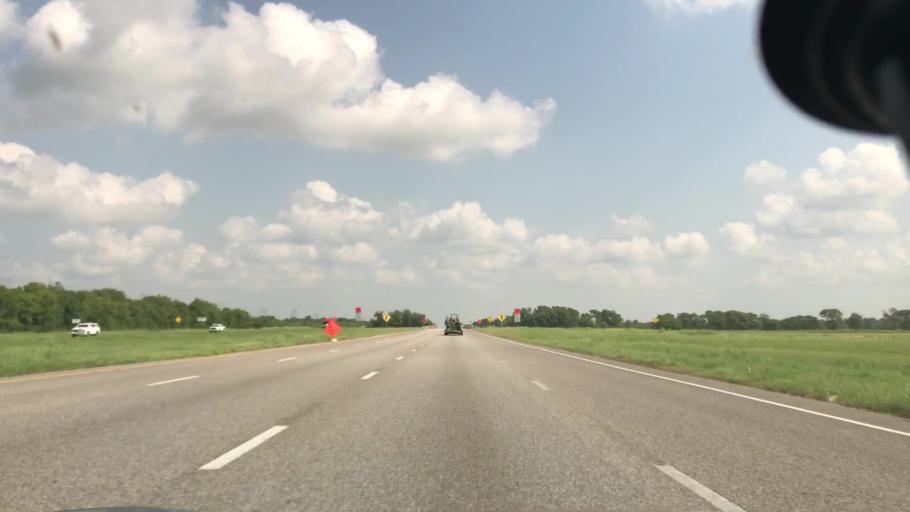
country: US
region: Texas
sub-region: Brazoria County
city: Rosharon
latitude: 29.3831
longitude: -95.4266
